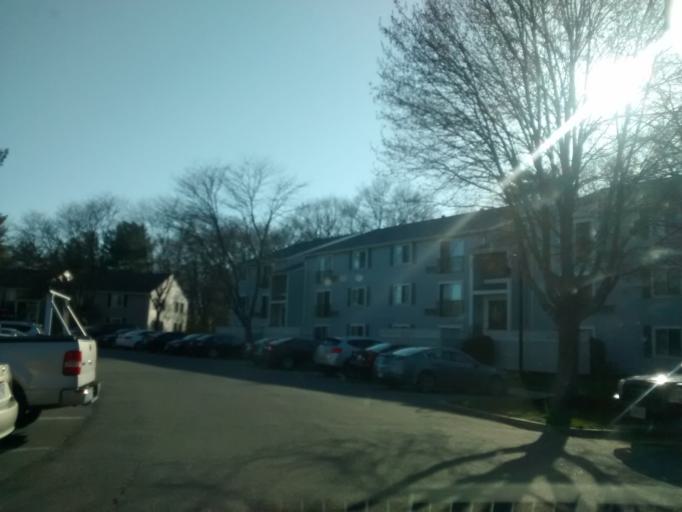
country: US
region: Massachusetts
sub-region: Middlesex County
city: Framingham
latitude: 42.2783
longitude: -71.3948
